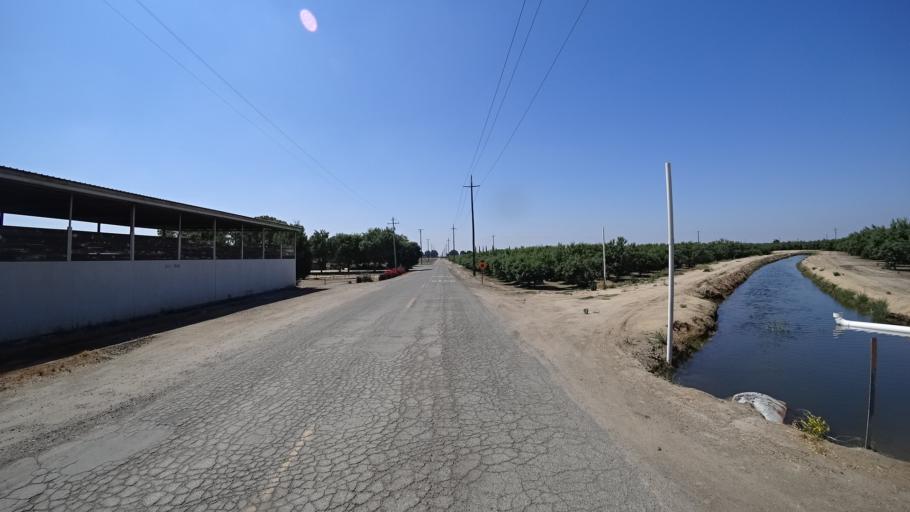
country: US
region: California
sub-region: Fresno County
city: Kingsburg
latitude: 36.4465
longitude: -119.5826
